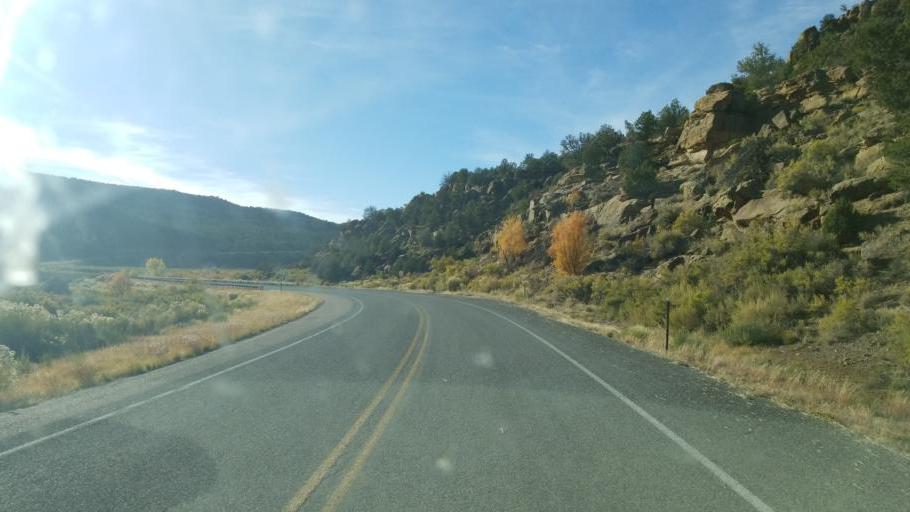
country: US
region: New Mexico
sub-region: Rio Arriba County
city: Navajo
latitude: 36.7107
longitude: -107.3065
